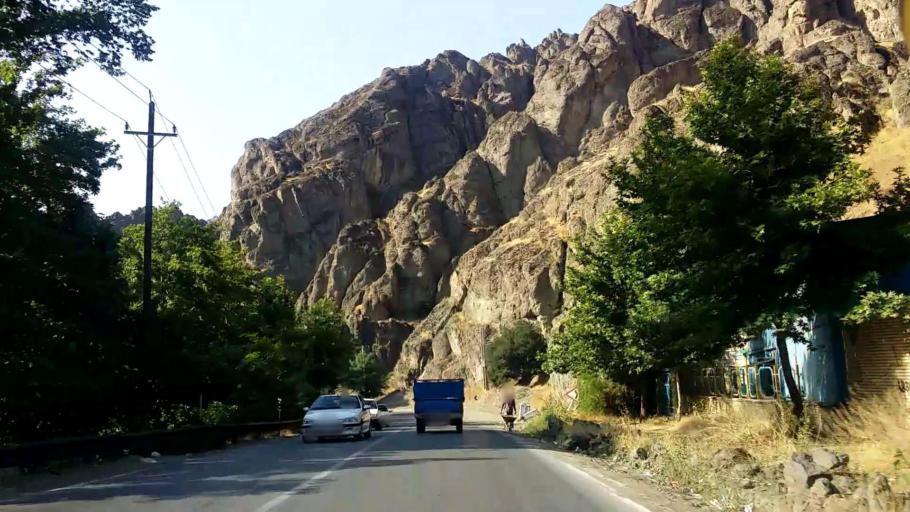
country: IR
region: Alborz
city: Karaj
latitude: 35.8802
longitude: 51.0415
